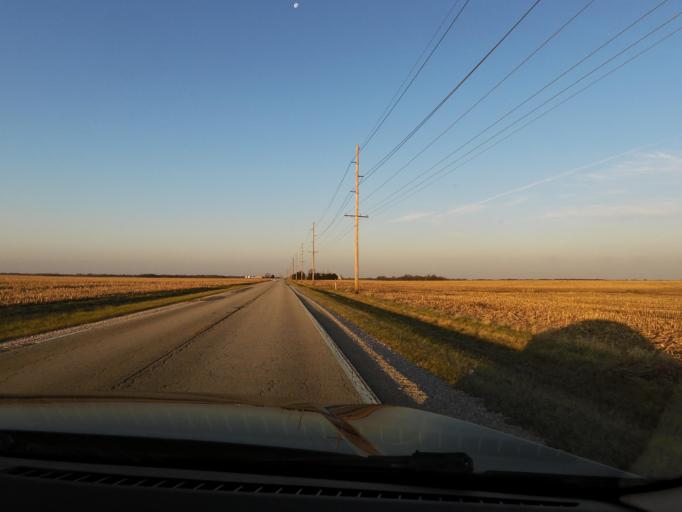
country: US
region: Illinois
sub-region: Marion County
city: Odin
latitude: 38.7653
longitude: -89.0178
